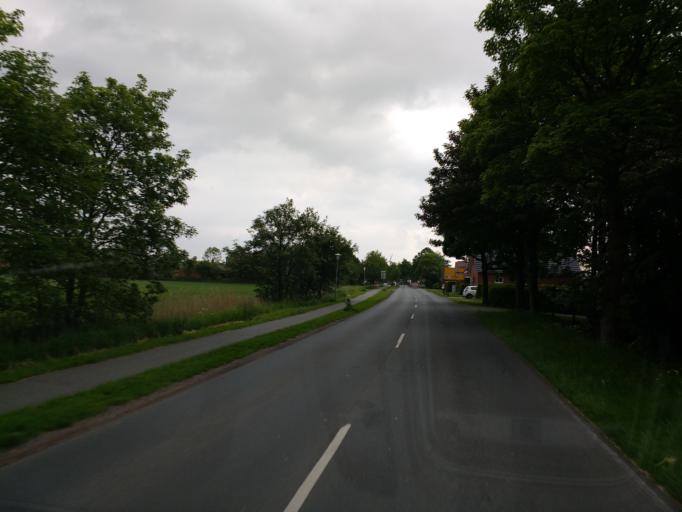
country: DE
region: Lower Saxony
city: Sillenstede
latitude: 53.6351
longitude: 8.0132
